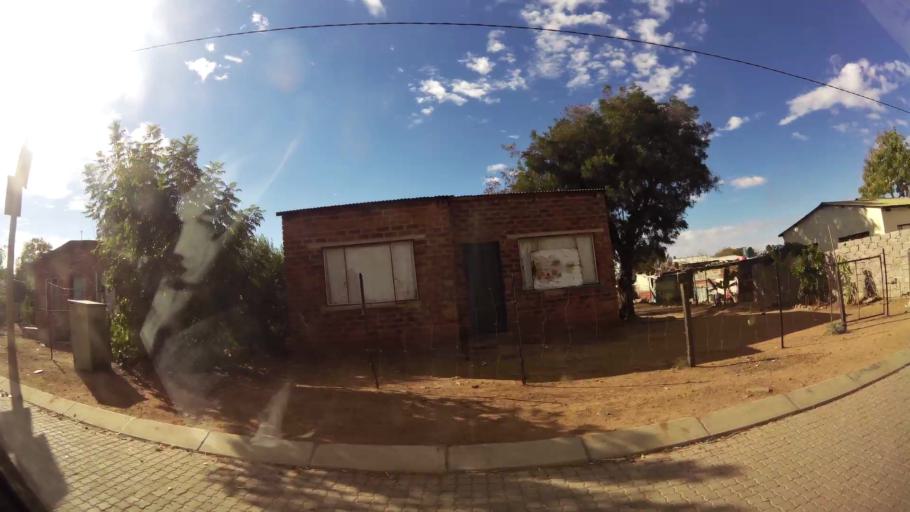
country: ZA
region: Limpopo
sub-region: Waterberg District Municipality
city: Warmbaths
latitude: -24.8759
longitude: 28.2710
